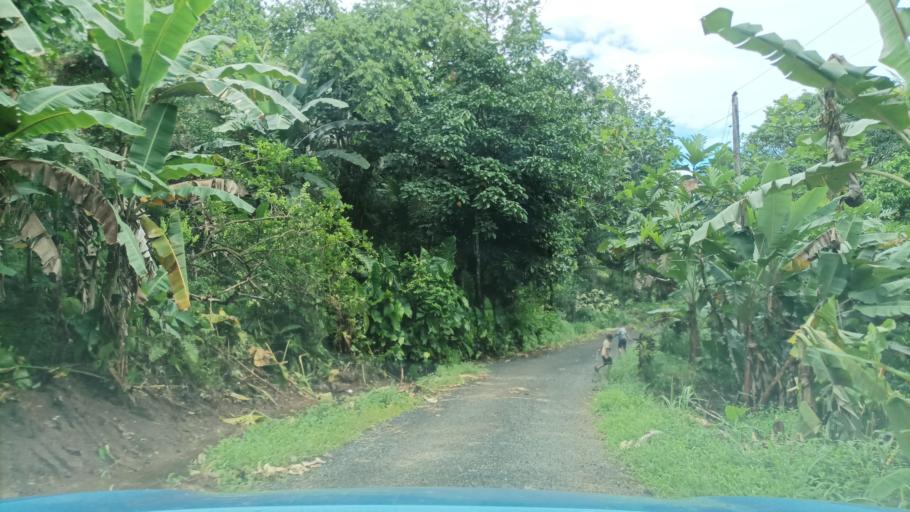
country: FM
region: Pohnpei
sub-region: Sokehs Municipality
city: Palikir - National Government Center
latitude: 6.8428
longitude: 158.1774
